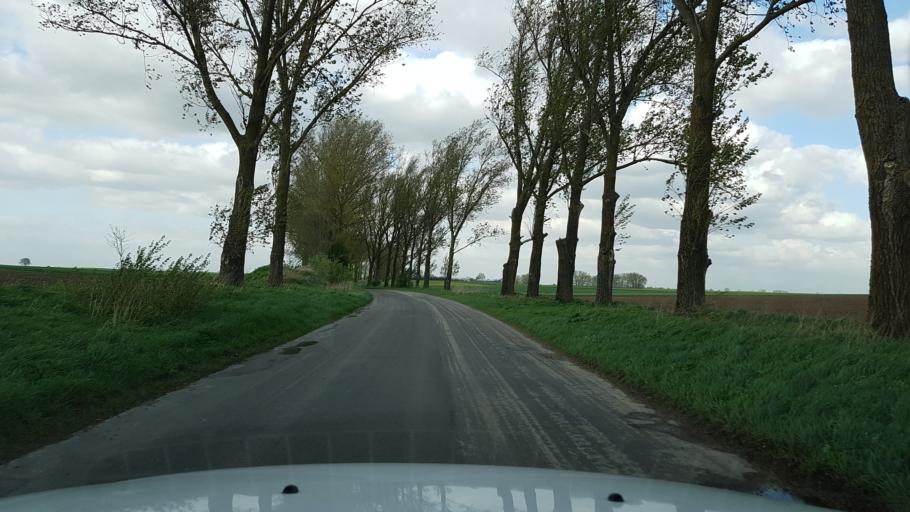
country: PL
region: West Pomeranian Voivodeship
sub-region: Powiat pyrzycki
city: Przelewice
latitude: 53.0338
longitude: 15.0817
